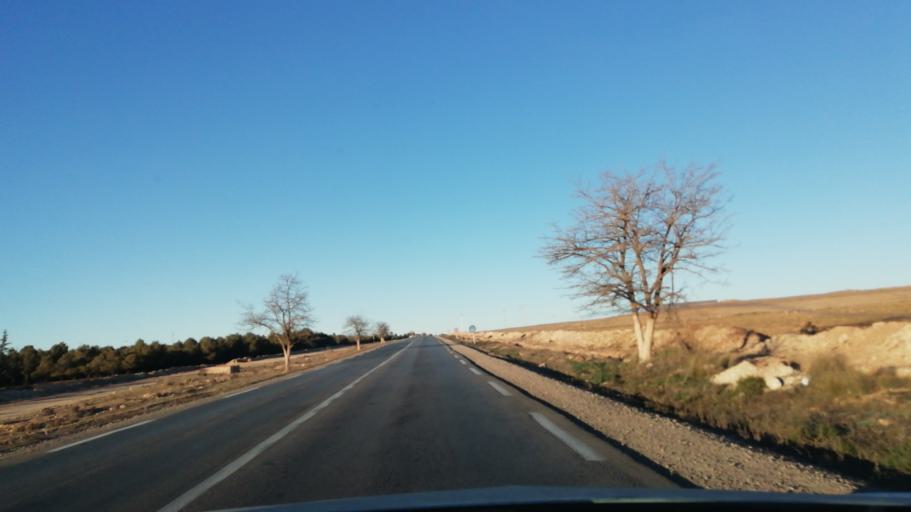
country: DZ
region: Saida
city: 'Ain el Hadjar
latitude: 34.5581
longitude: 0.1184
